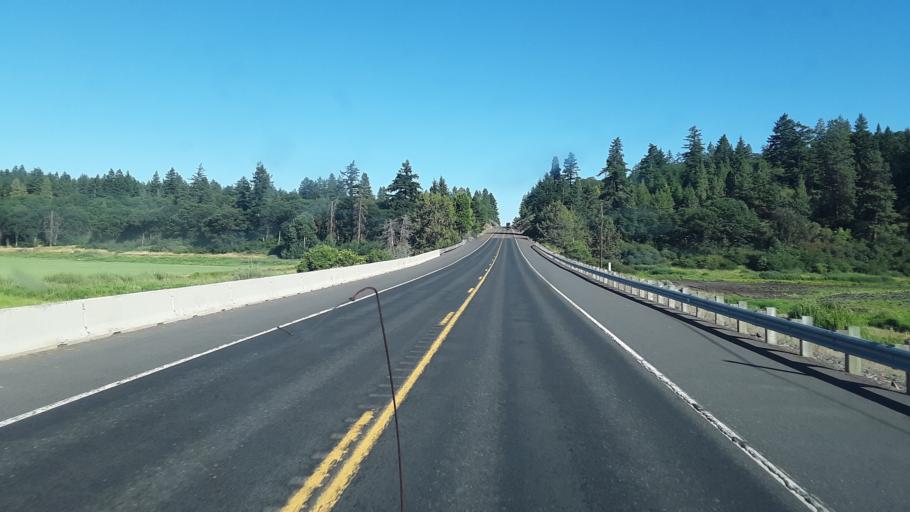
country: US
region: Oregon
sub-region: Klamath County
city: Klamath Falls
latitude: 42.2847
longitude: -121.9198
